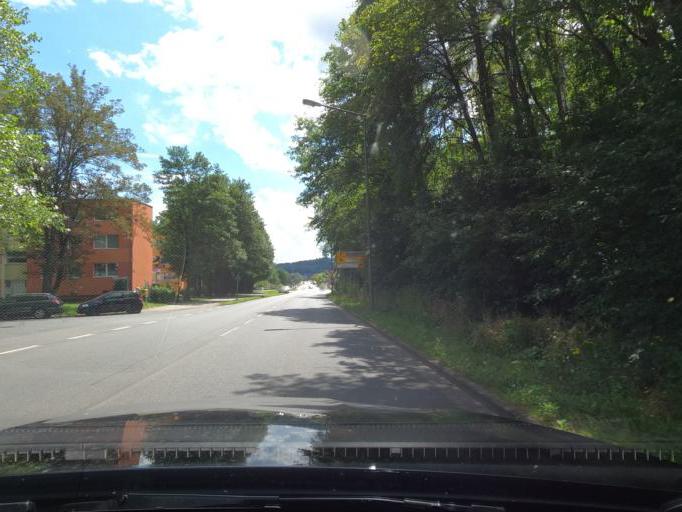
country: DE
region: Lower Saxony
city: Elbe
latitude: 52.1410
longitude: 10.2937
